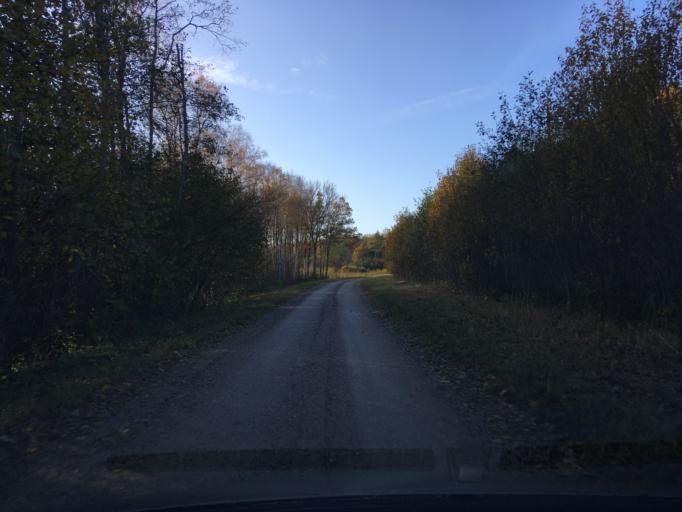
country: EE
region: Laeaene
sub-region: Lihula vald
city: Lihula
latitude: 58.5682
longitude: 23.7563
